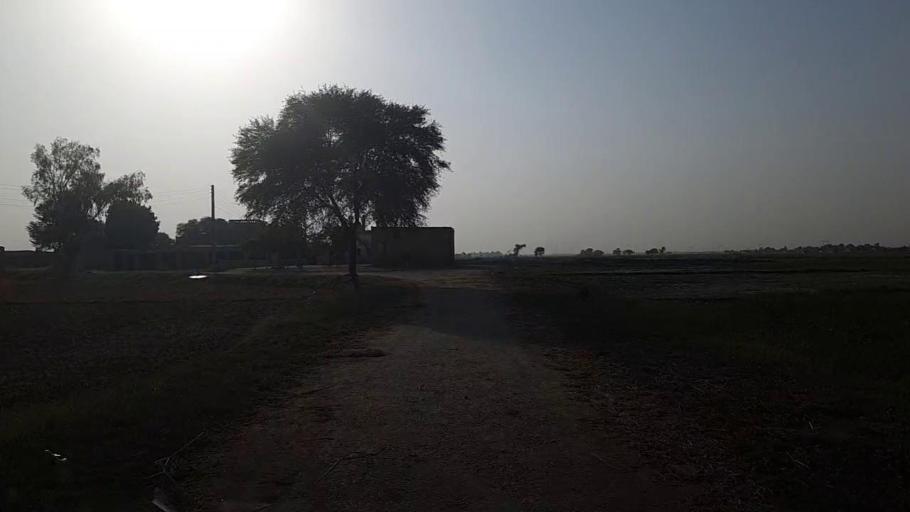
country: PK
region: Sindh
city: Kandhkot
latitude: 28.2500
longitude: 69.1572
